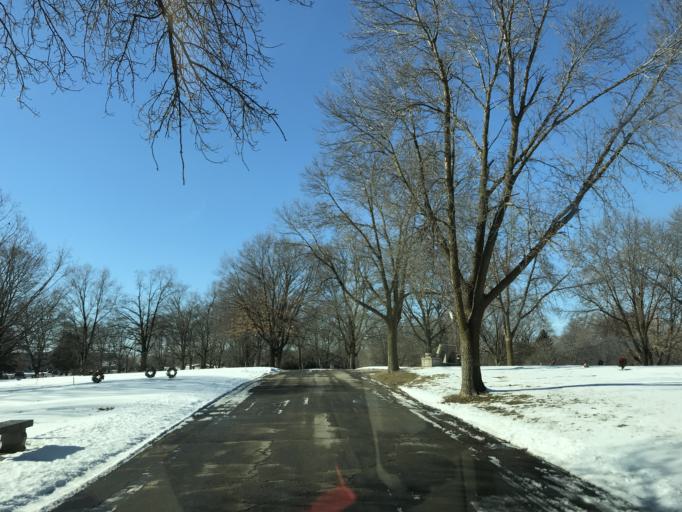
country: US
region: Wisconsin
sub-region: Dane County
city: Monona
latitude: 43.0488
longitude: -89.3201
